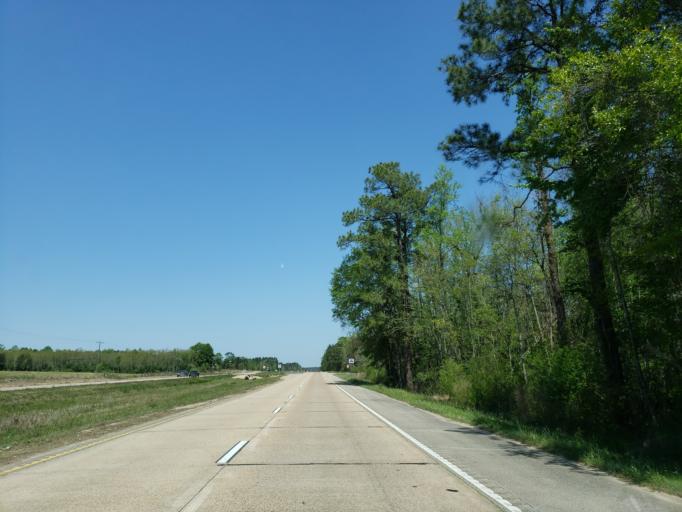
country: US
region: Mississippi
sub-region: Lamar County
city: Purvis
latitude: 31.0749
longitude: -89.2099
